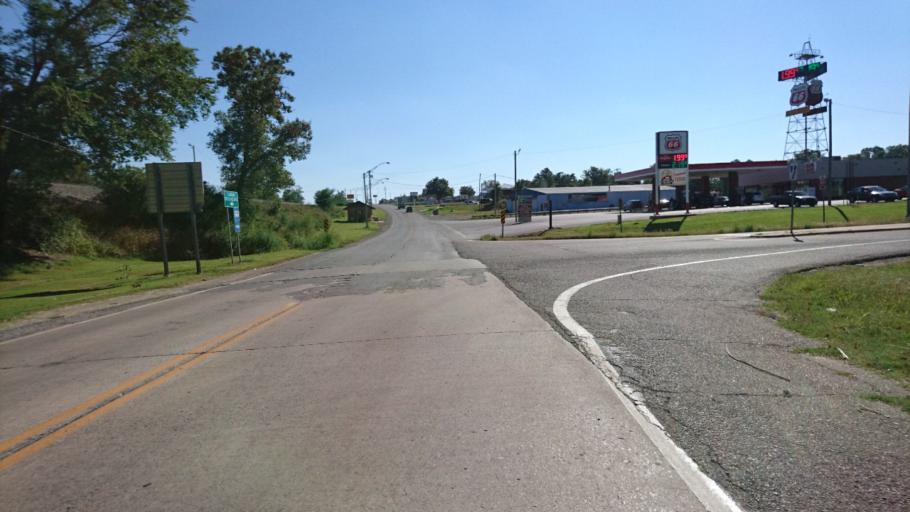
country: US
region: Oklahoma
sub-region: Custer County
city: Clinton
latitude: 35.4973
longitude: -98.9777
